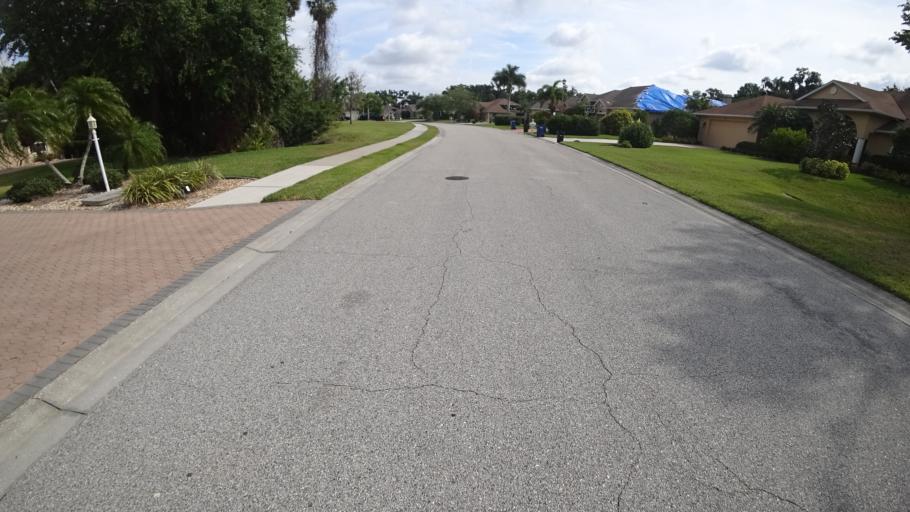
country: US
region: Florida
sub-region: Manatee County
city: Ellenton
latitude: 27.5644
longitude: -82.4731
